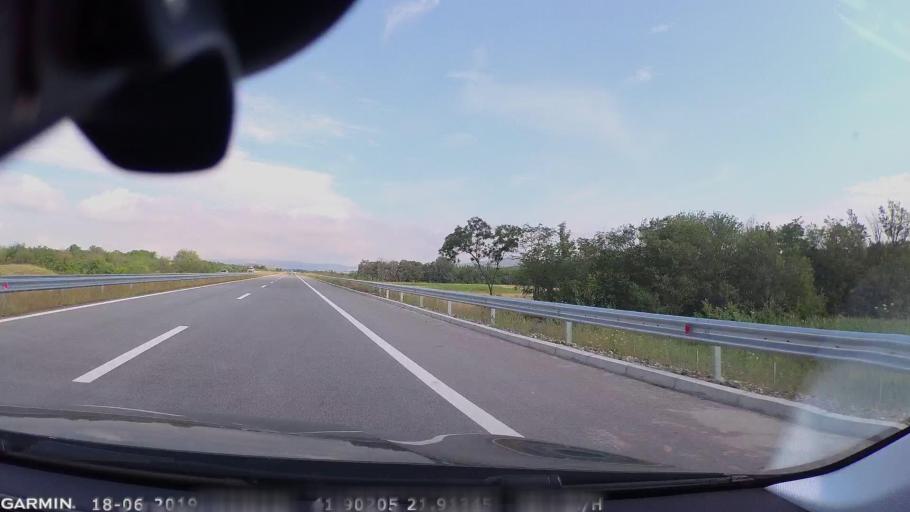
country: MK
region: Sveti Nikole
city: Gorobinci
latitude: 41.9033
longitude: 21.9117
